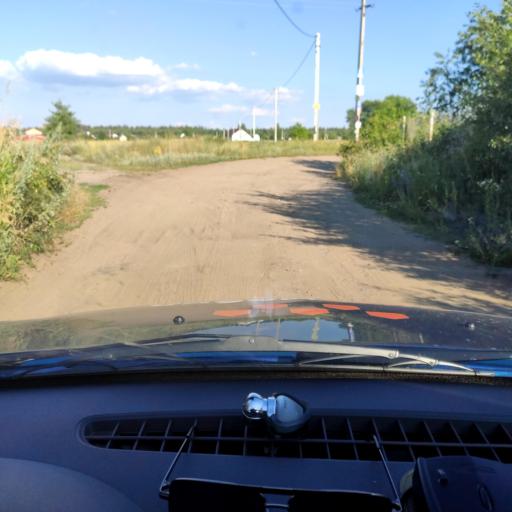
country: RU
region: Voronezj
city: Podgornoye
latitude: 51.8662
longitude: 39.1735
